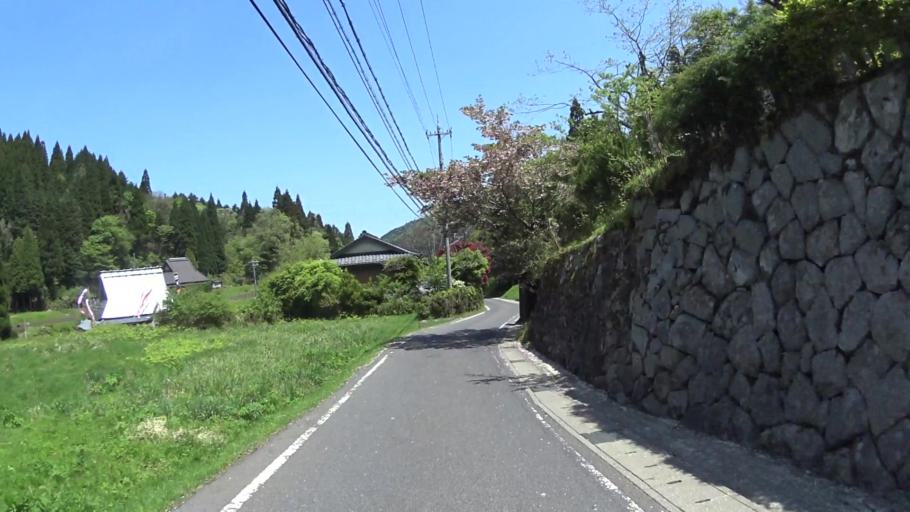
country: JP
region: Shiga Prefecture
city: Kitahama
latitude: 35.1661
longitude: 135.7834
